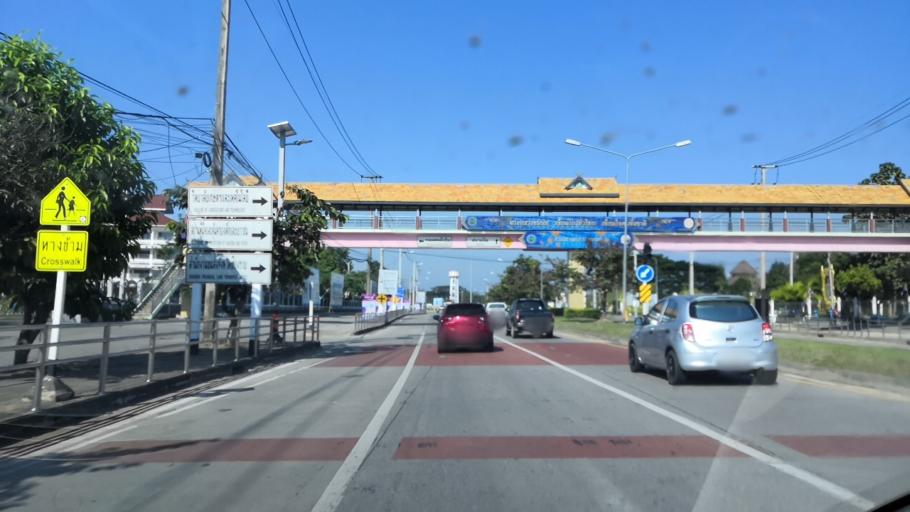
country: TH
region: Chiang Rai
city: Chiang Rai
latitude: 19.9279
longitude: 99.8632
